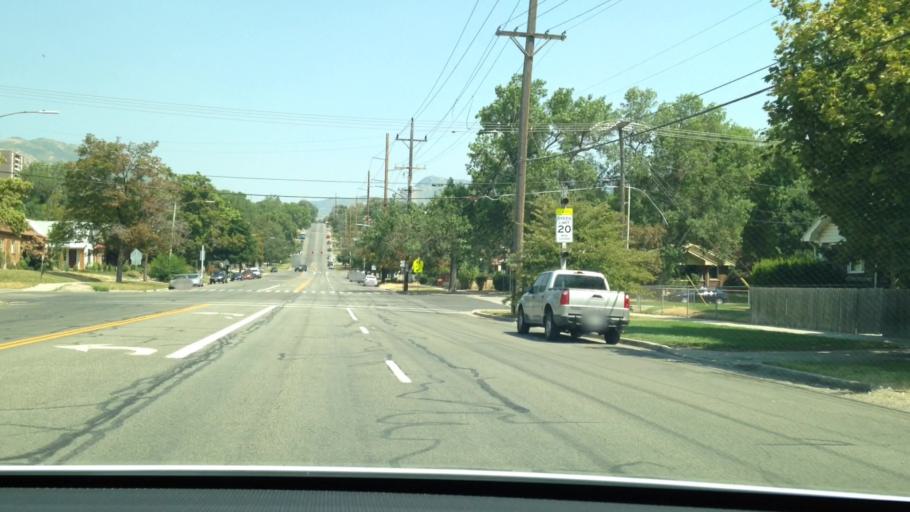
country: US
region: Utah
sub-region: Salt Lake County
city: Salt Lake City
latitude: 40.7563
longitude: -111.8690
